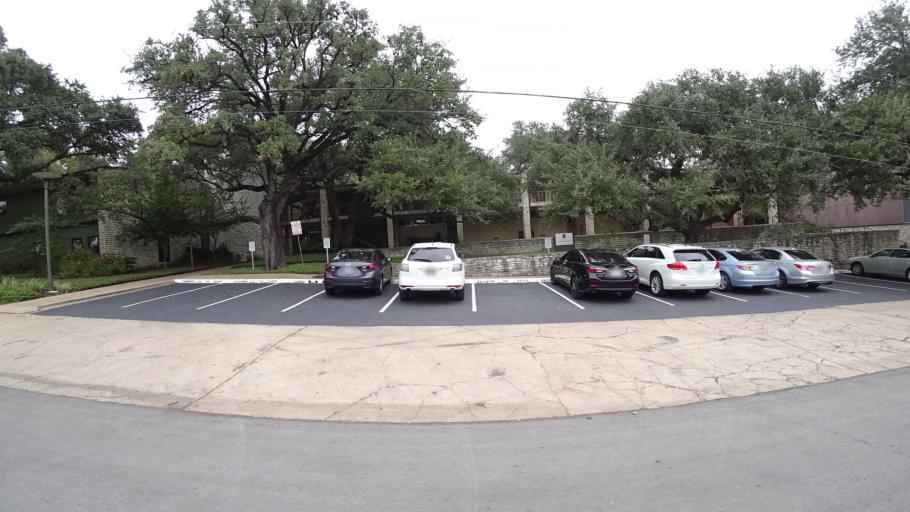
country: US
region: Texas
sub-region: Travis County
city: Austin
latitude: 30.2922
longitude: -97.7326
